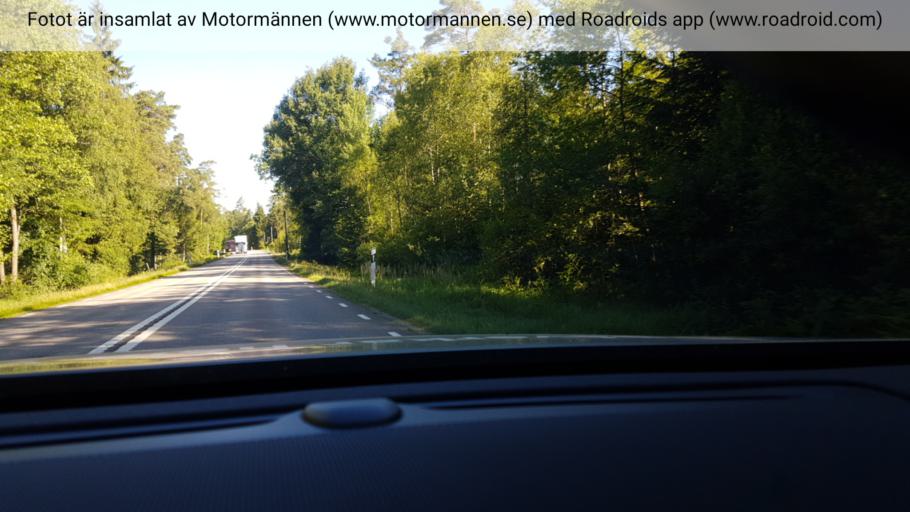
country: SE
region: Kronoberg
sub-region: Markaryds Kommun
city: Markaryd
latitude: 56.4087
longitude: 13.6414
